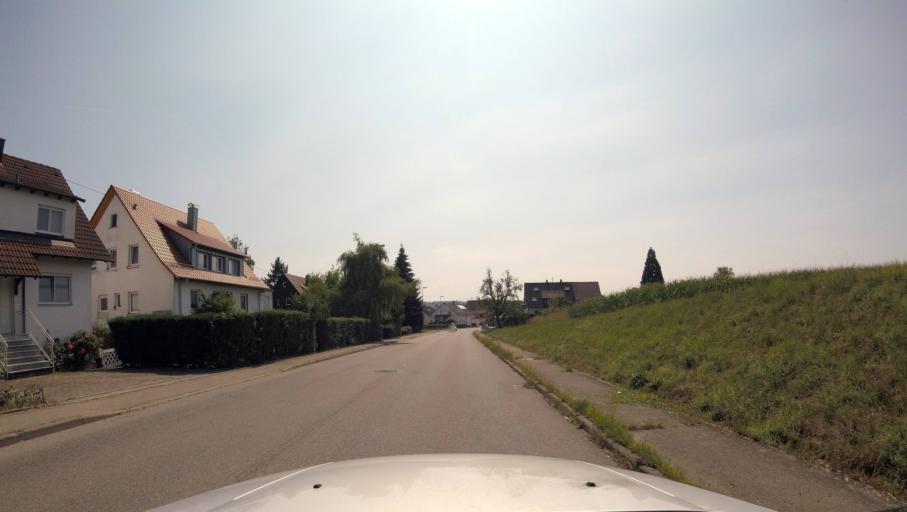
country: DE
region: Baden-Wuerttemberg
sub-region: Regierungsbezirk Stuttgart
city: Oppenweiler
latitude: 48.9500
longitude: 9.4999
